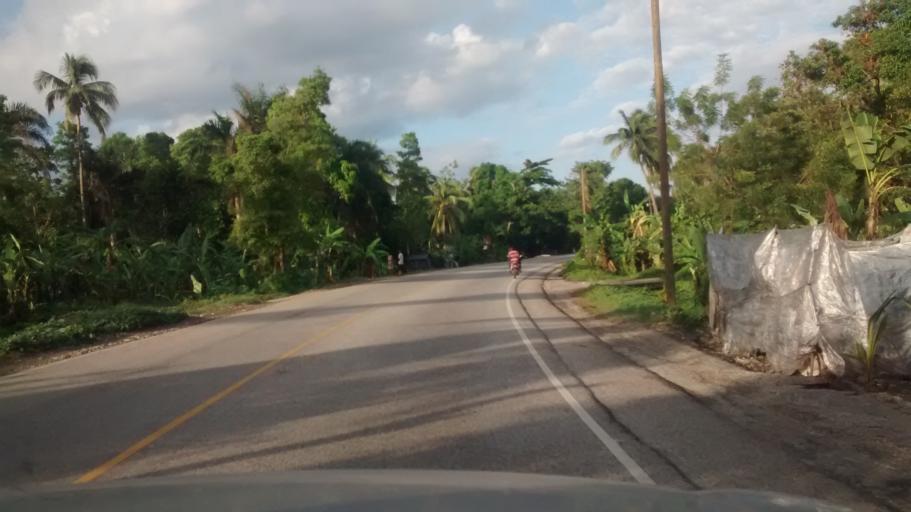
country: HT
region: Ouest
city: Tigwav
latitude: 18.4207
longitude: -72.9090
